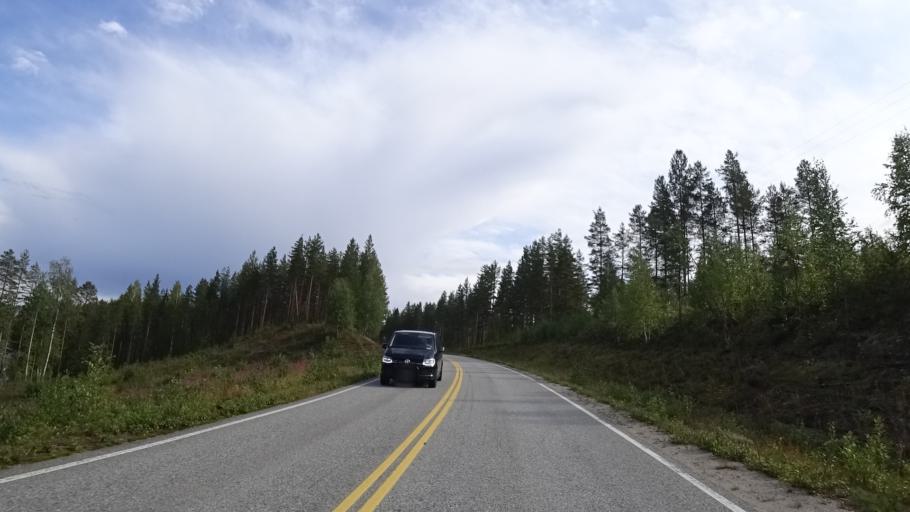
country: FI
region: North Karelia
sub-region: Joensuu
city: Ilomantsi
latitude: 62.6292
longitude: 31.0946
